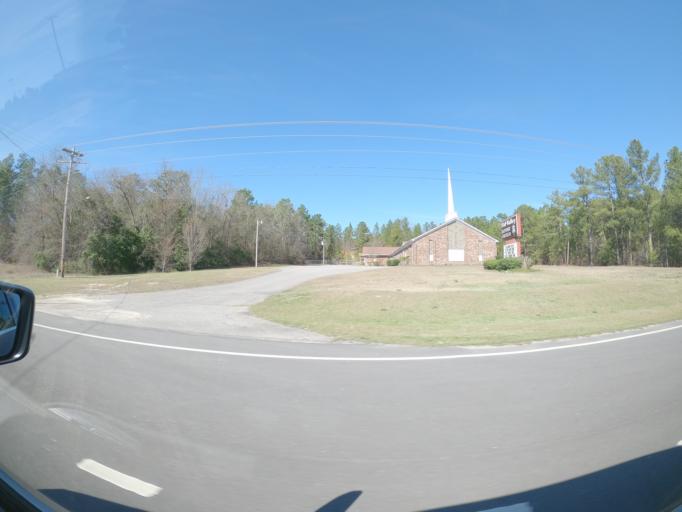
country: US
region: South Carolina
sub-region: Aiken County
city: Langley
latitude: 33.5276
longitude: -81.8466
